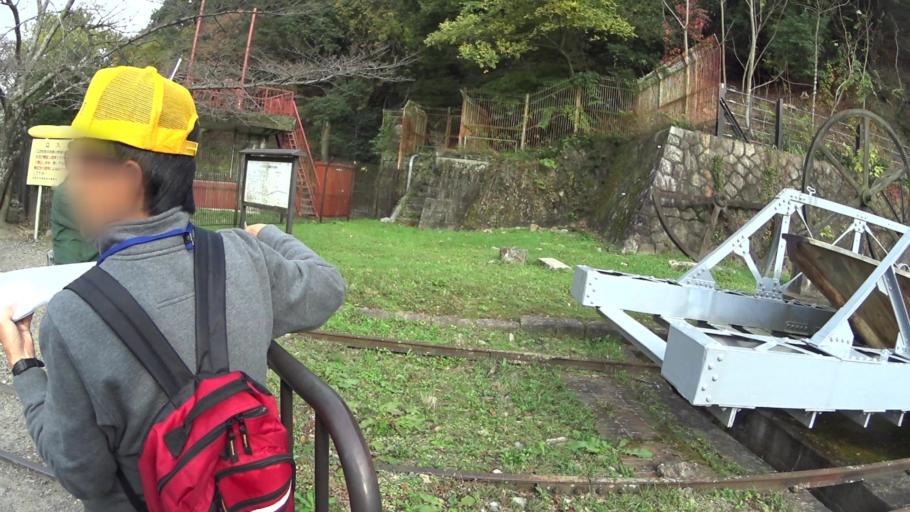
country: JP
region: Kyoto
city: Kyoto
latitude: 35.0074
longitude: 135.7914
